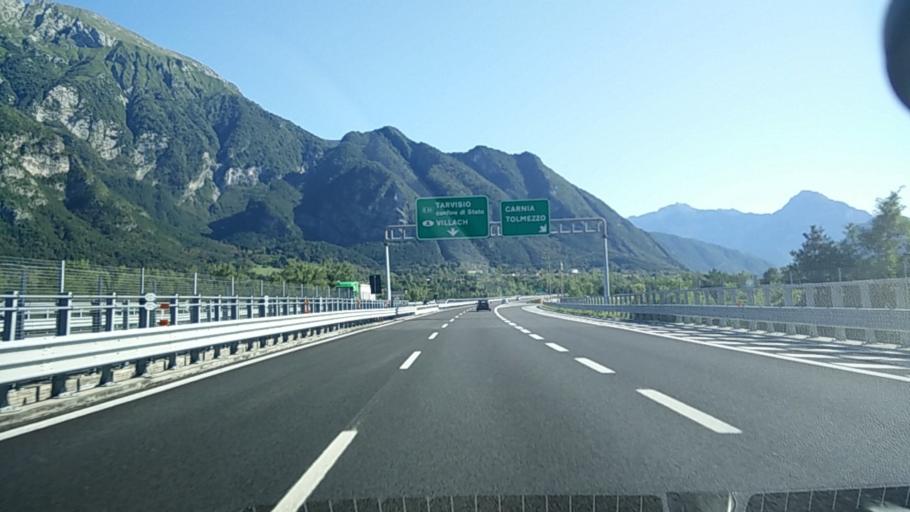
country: IT
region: Friuli Venezia Giulia
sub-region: Provincia di Udine
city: Amaro
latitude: 46.3627
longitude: 13.0743
